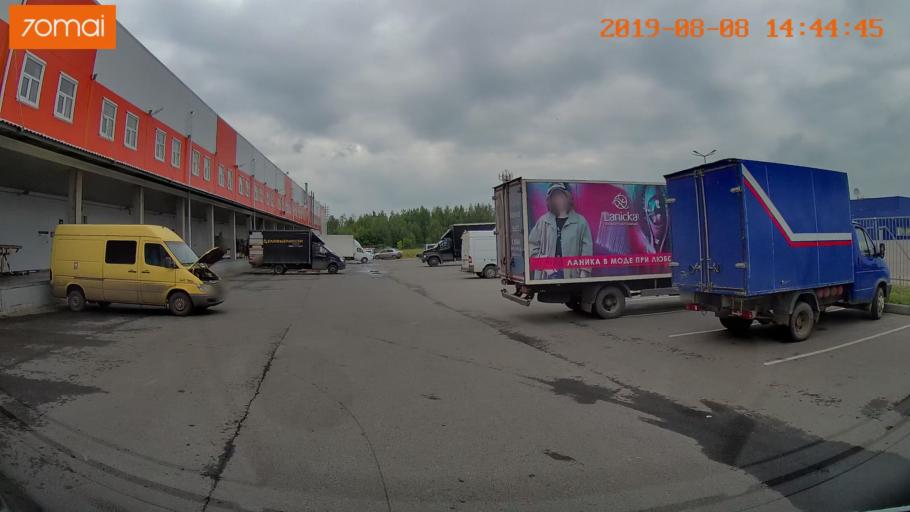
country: RU
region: Ivanovo
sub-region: Gorod Ivanovo
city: Ivanovo
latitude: 56.9501
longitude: 40.9573
